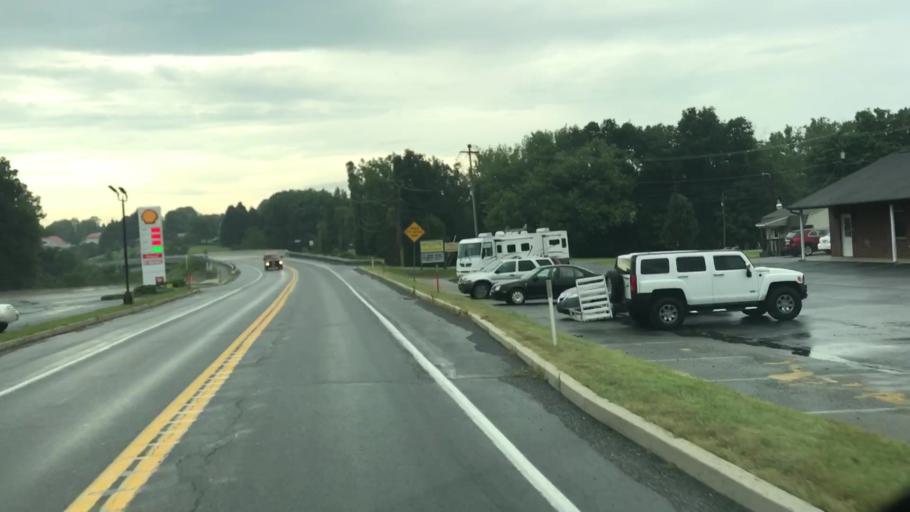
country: US
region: Pennsylvania
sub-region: Cumberland County
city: Schlusser
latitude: 40.3218
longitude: -77.1674
